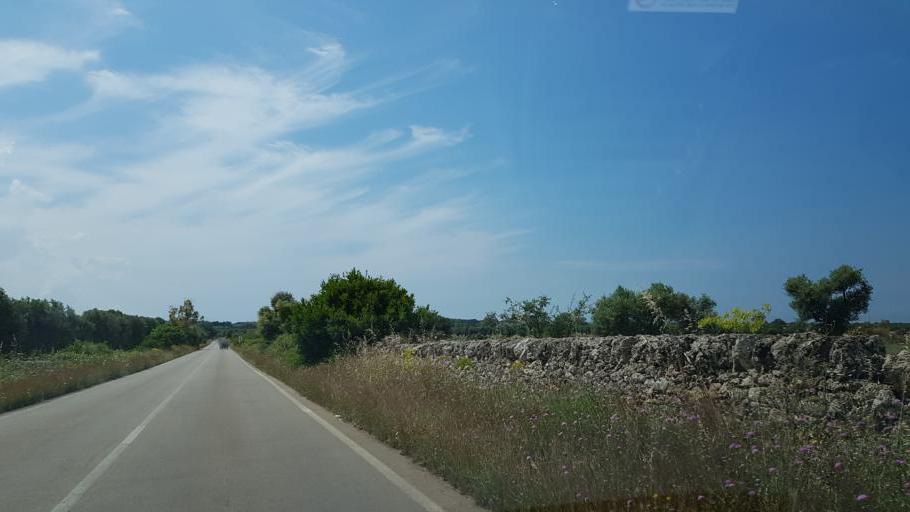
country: IT
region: Apulia
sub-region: Provincia di Lecce
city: Porto Cesareo
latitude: 40.3155
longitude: 17.8613
